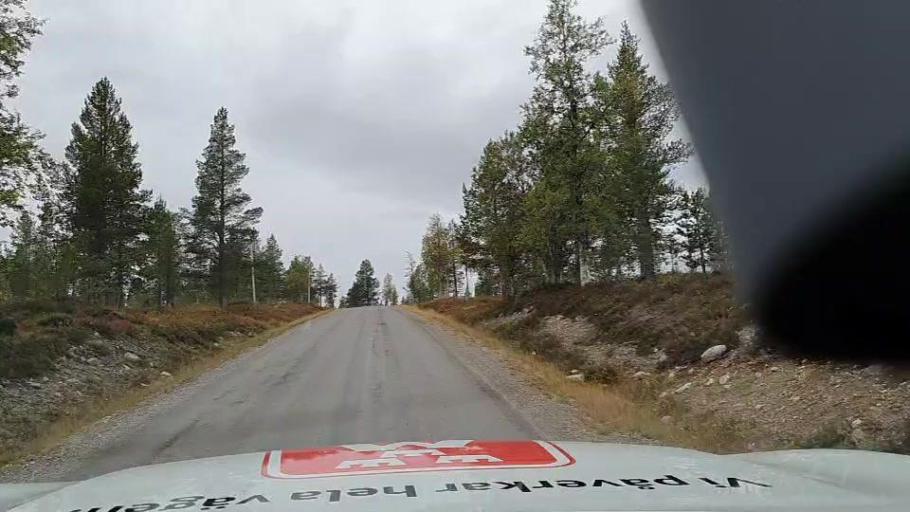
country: NO
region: Hedmark
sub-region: Engerdal
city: Engerdal
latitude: 62.1265
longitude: 12.8779
